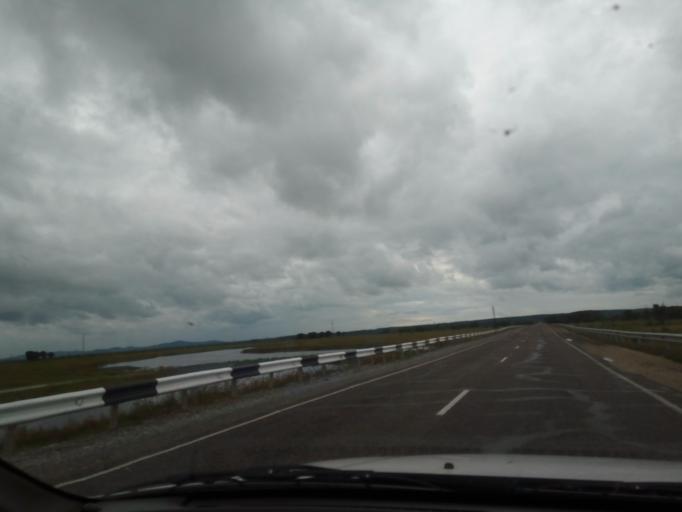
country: RU
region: Primorskiy
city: Dal'nerechensk
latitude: 45.9129
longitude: 133.7665
